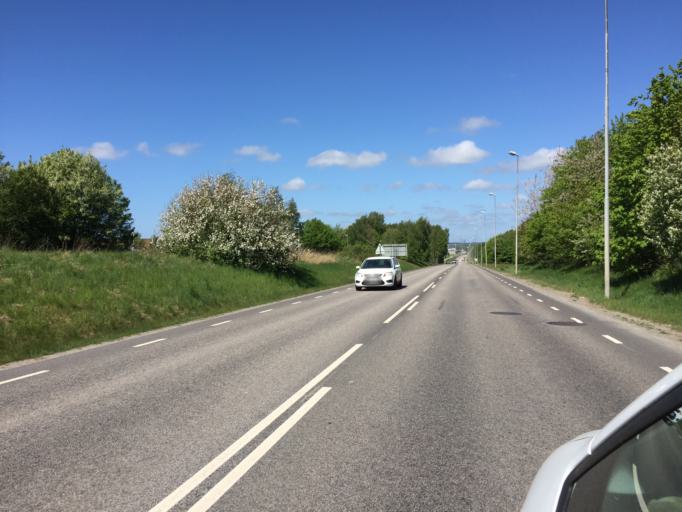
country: SE
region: Halland
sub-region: Varbergs Kommun
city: Varberg
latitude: 57.1125
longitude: 12.2918
